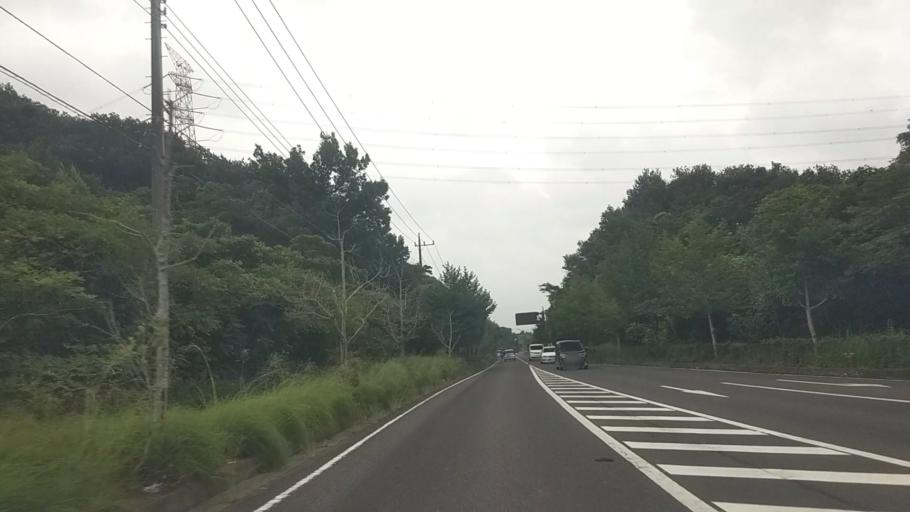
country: JP
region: Chiba
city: Kisarazu
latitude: 35.3862
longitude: 140.0019
